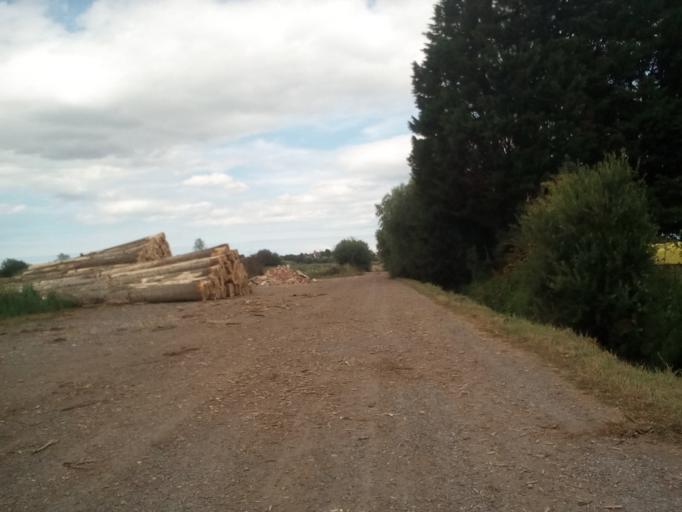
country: FR
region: Lower Normandy
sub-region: Departement du Calvados
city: Troarn
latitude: 49.1739
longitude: -0.1653
